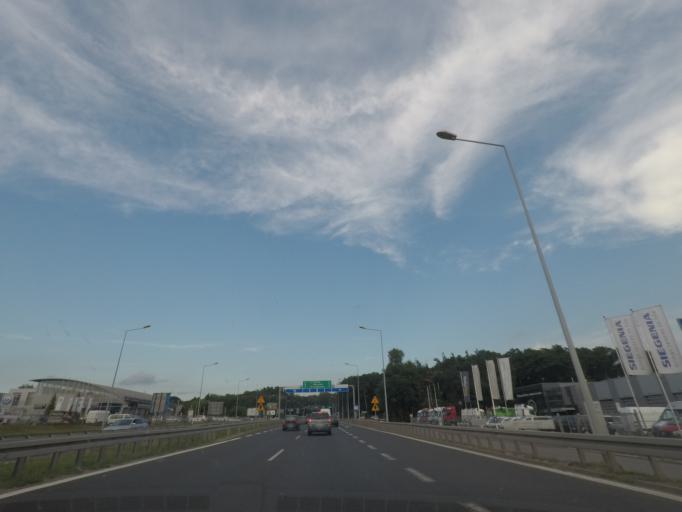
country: PL
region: Lesser Poland Voivodeship
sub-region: Powiat krakowski
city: Rzaska
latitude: 50.1066
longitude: 19.8473
